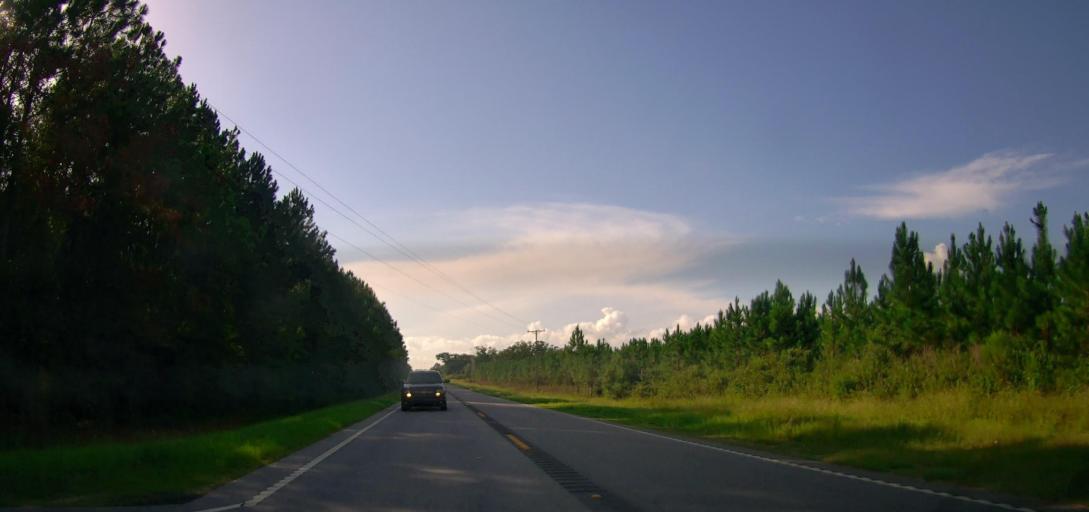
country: US
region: Georgia
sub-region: Coffee County
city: Nicholls
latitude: 31.4265
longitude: -82.6991
